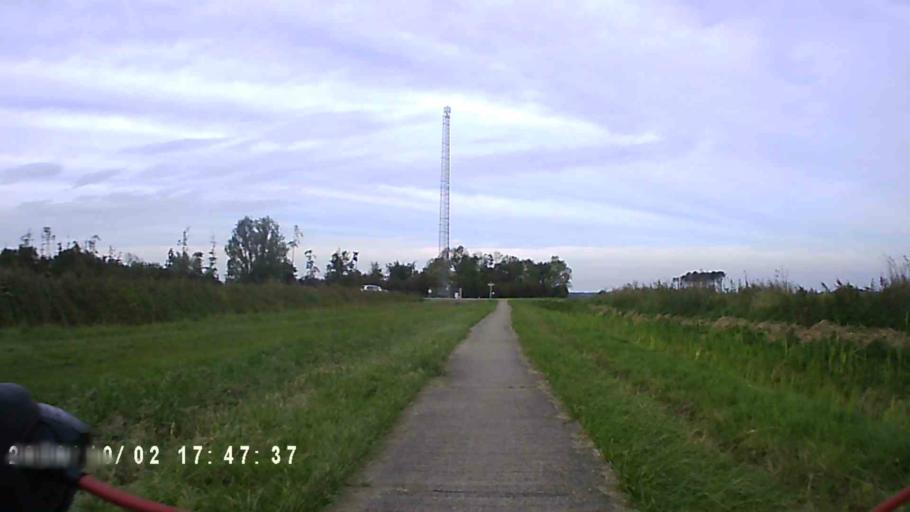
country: NL
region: Groningen
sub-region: Gemeente Zuidhorn
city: Oldehove
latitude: 53.3378
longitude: 6.3976
